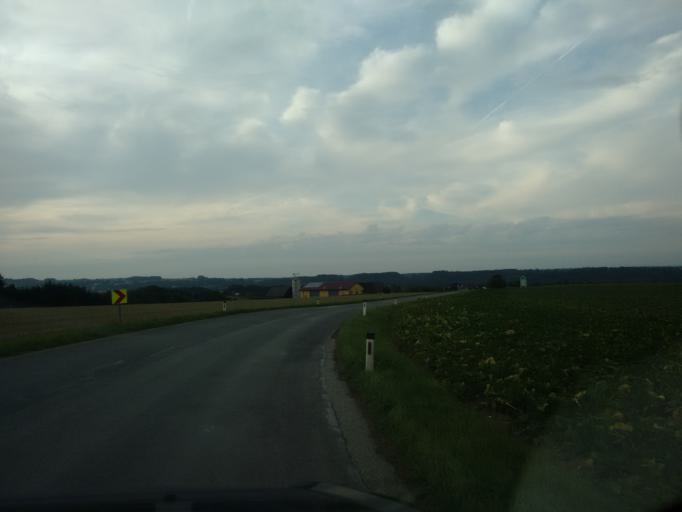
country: AT
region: Upper Austria
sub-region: Politischer Bezirk Steyr-Land
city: Pfarrkirchen bei Bad Hall
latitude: 48.0463
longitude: 14.1803
